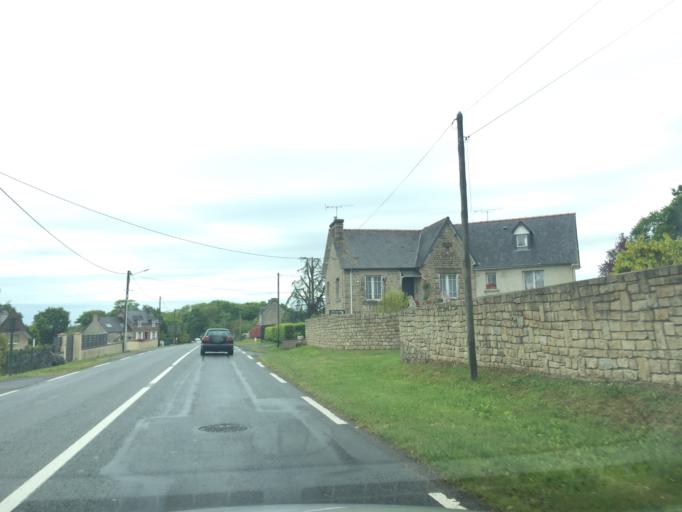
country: FR
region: Brittany
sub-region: Departement des Cotes-d'Armor
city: Ploubalay
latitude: 48.5708
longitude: -2.1805
